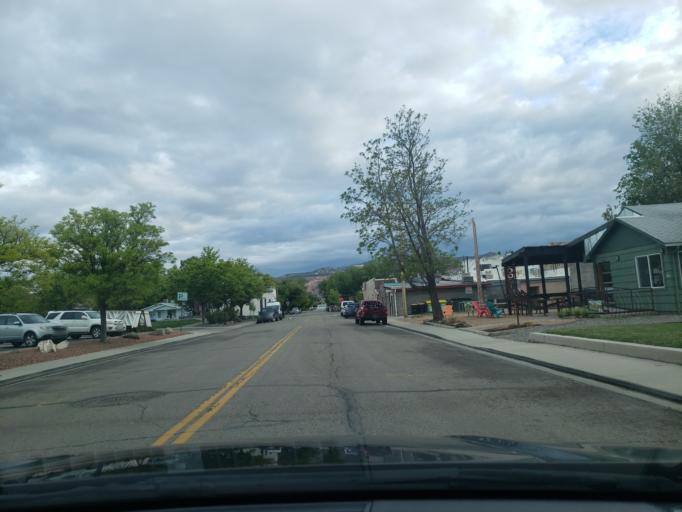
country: US
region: Colorado
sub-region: Mesa County
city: Fruita
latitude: 39.1598
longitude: -108.7314
